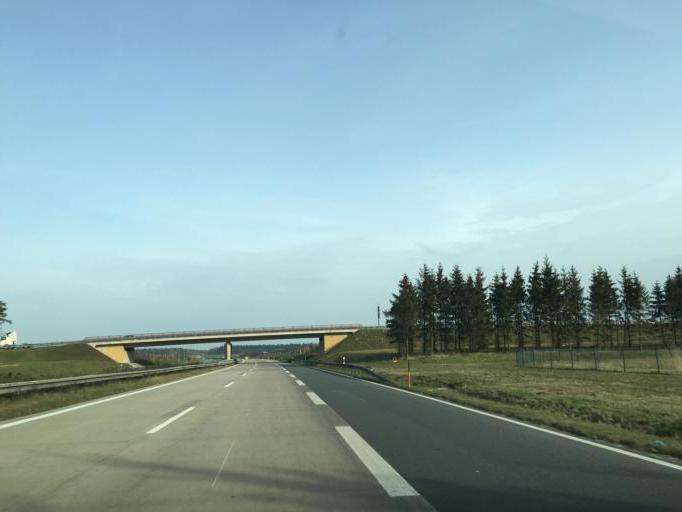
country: DE
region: Mecklenburg-Vorpommern
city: Malchow
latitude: 53.3664
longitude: 12.4687
